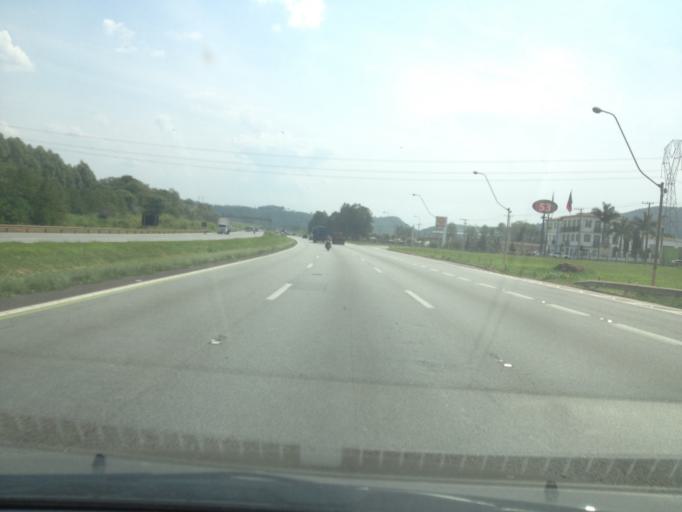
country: BR
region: Sao Paulo
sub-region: Pirapora Do Bom Jesus
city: Pirapora do Bom Jesus
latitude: -23.4363
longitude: -47.0951
